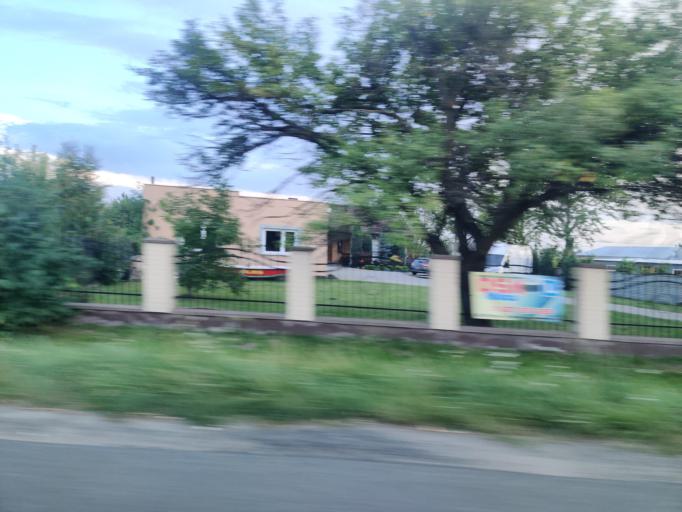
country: PL
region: Greater Poland Voivodeship
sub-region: Konin
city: Konin
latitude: 52.1946
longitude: 18.3132
